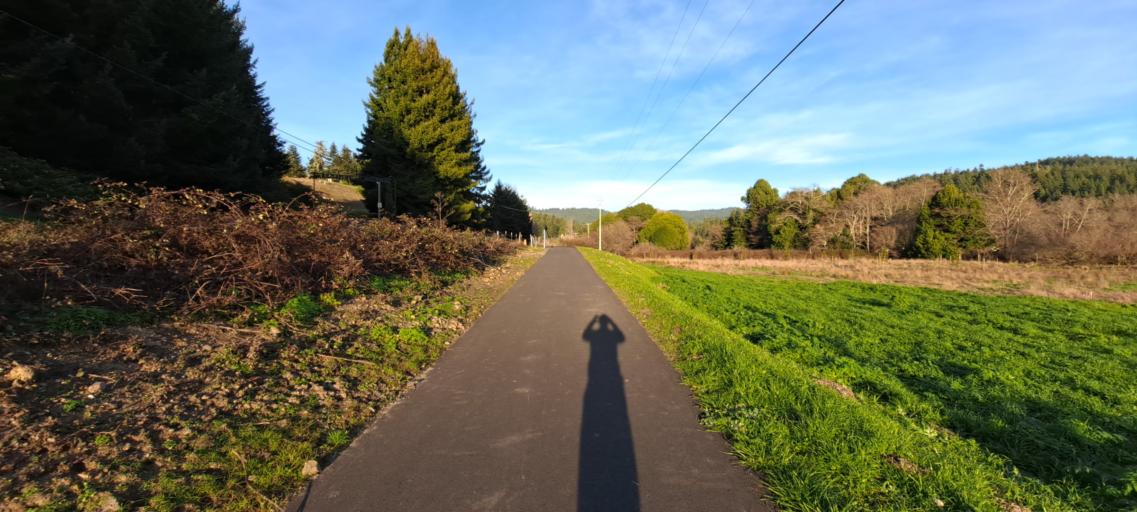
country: US
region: California
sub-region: Humboldt County
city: Fortuna
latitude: 40.5955
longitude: -124.1325
